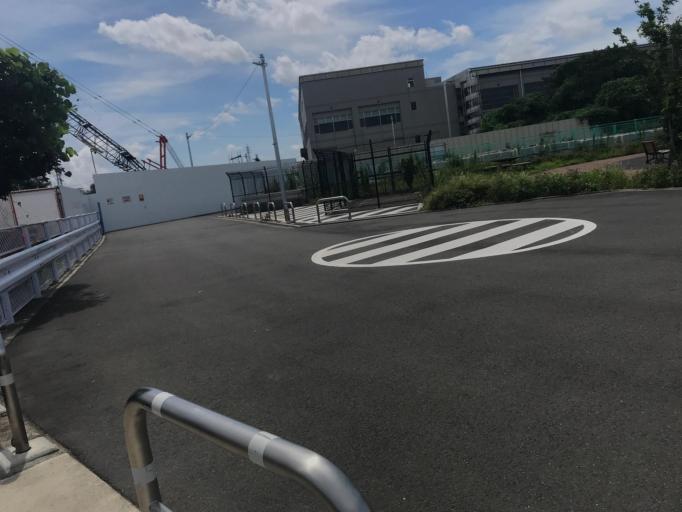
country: JP
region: Tokyo
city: Tanashicho
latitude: 35.7629
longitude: 139.5456
